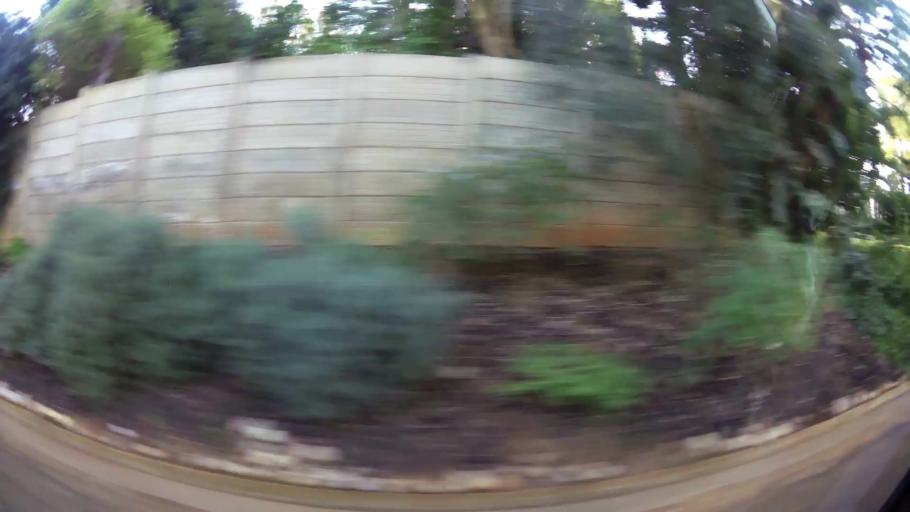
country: ZA
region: Western Cape
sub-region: Eden District Municipality
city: Riversdale
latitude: -34.0838
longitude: 20.9574
